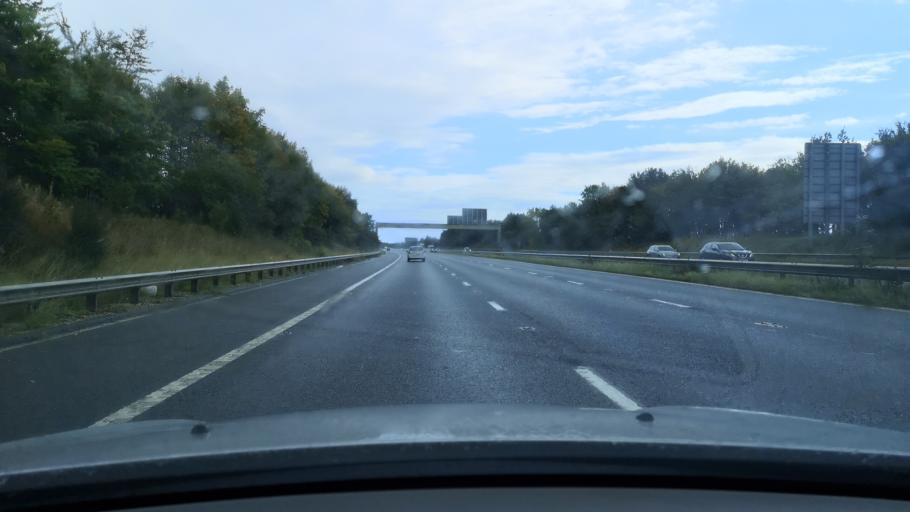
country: GB
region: England
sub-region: City and Borough of Wakefield
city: Knottingley
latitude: 53.6928
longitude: -1.2476
